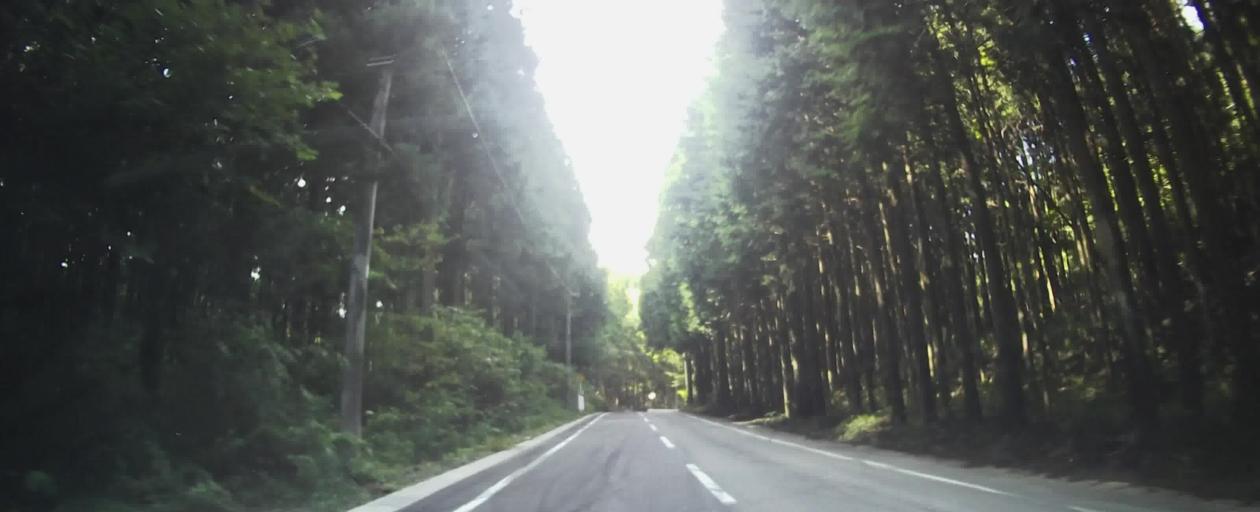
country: JP
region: Gunma
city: Kanekomachi
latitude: 36.4440
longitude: 138.9082
